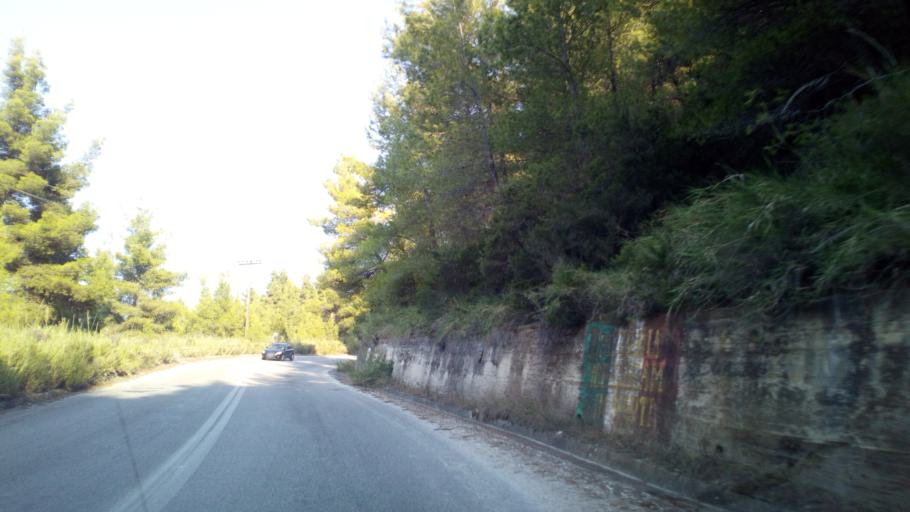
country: GR
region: Central Macedonia
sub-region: Nomos Chalkidikis
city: Neos Marmaras
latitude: 40.1752
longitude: 23.8396
